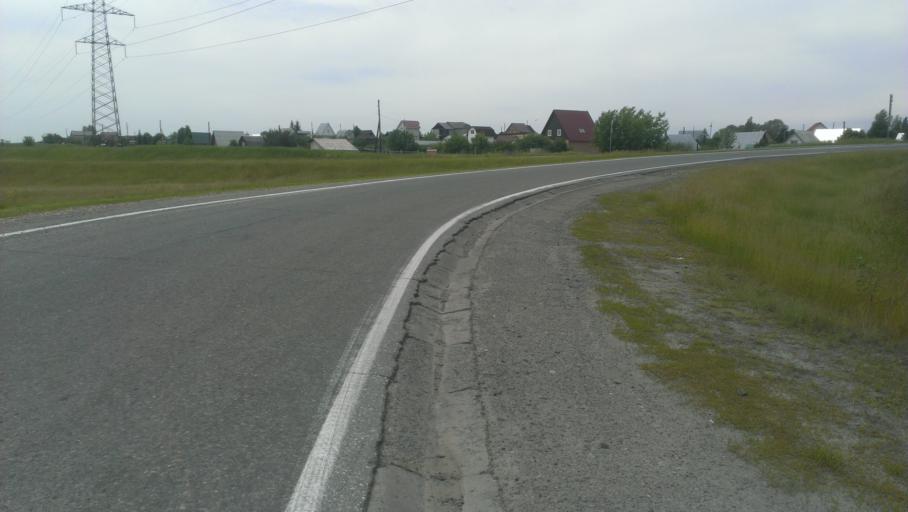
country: RU
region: Altai Krai
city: Sannikovo
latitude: 53.3403
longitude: 83.9349
